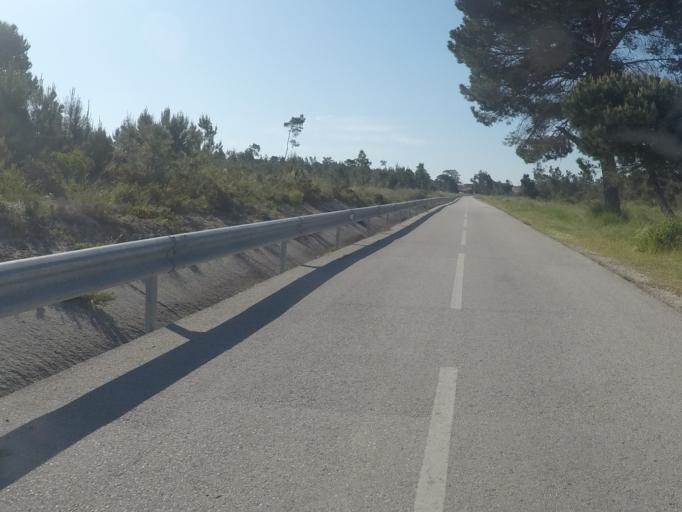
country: PT
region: Setubal
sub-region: Sesimbra
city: Sesimbra
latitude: 38.4843
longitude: -9.1635
